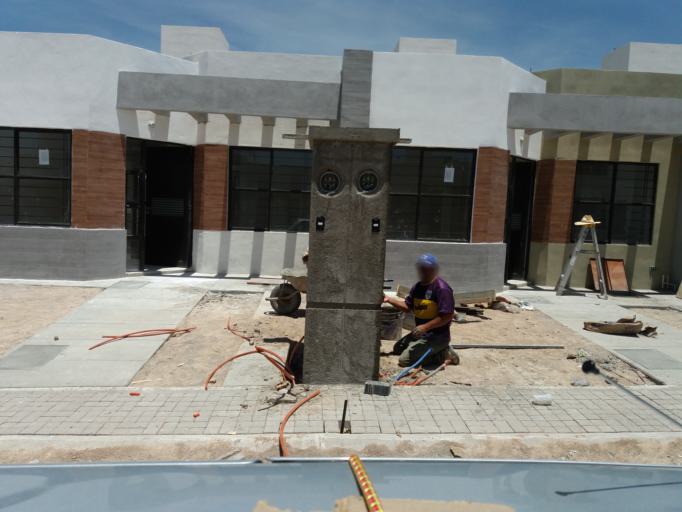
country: MX
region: Aguascalientes
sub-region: Aguascalientes
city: San Sebastian [Fraccionamiento]
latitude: 21.8116
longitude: -102.3048
